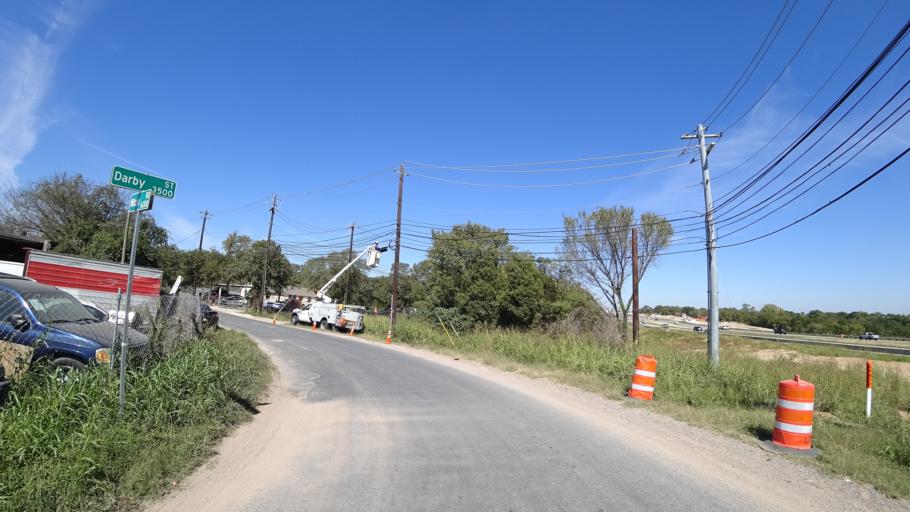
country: US
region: Texas
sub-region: Travis County
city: Austin
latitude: 30.2710
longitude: -97.6699
